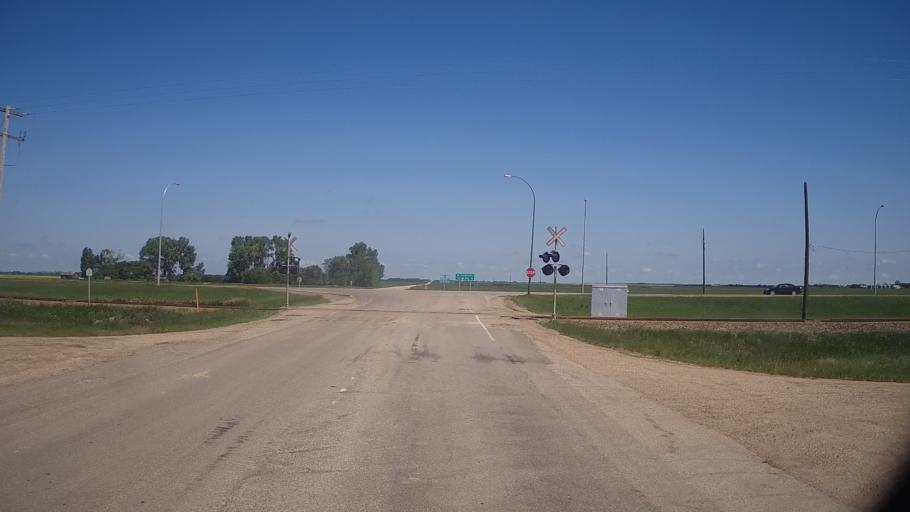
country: CA
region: Saskatchewan
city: Saskatoon
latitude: 51.9904
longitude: -106.0755
